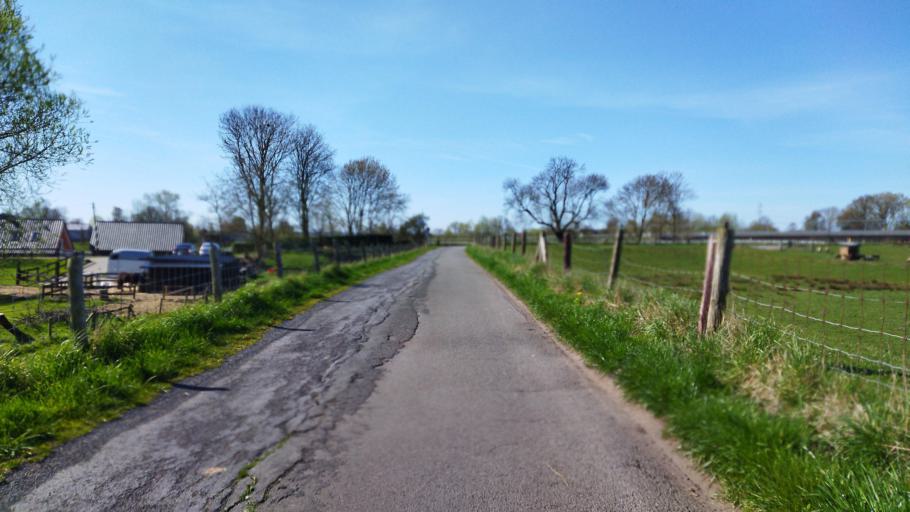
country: DE
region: Lower Saxony
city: Elsfleth
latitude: 53.2008
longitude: 8.4514
